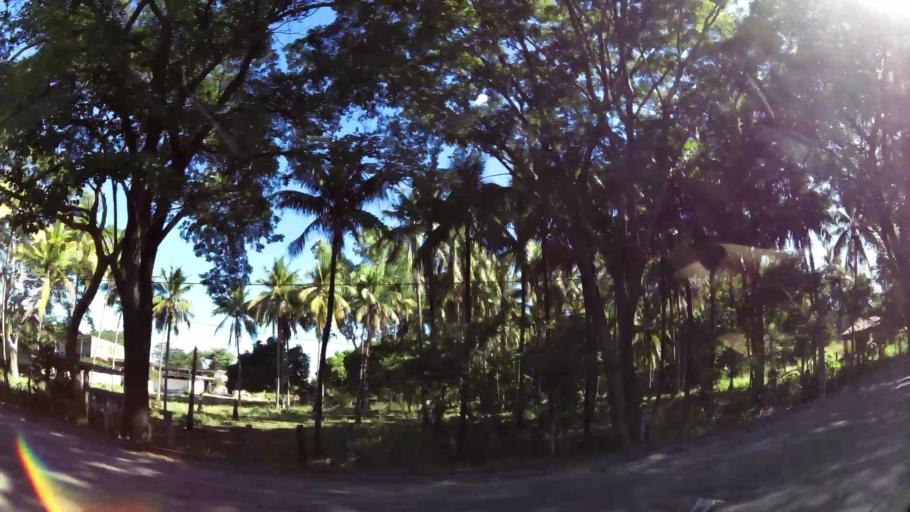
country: SV
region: San Miguel
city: San Miguel
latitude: 13.4534
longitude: -88.1399
